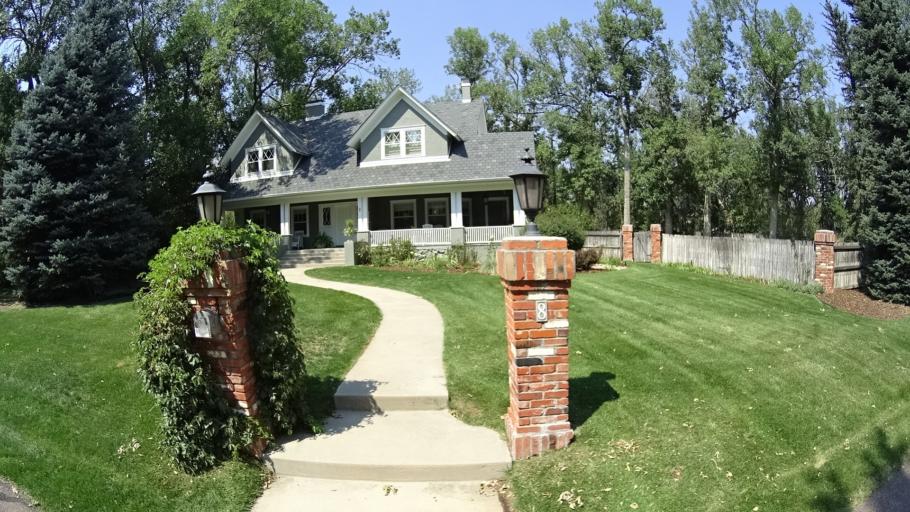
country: US
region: Colorado
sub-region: El Paso County
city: Colorado Springs
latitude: 38.7897
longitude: -104.8454
